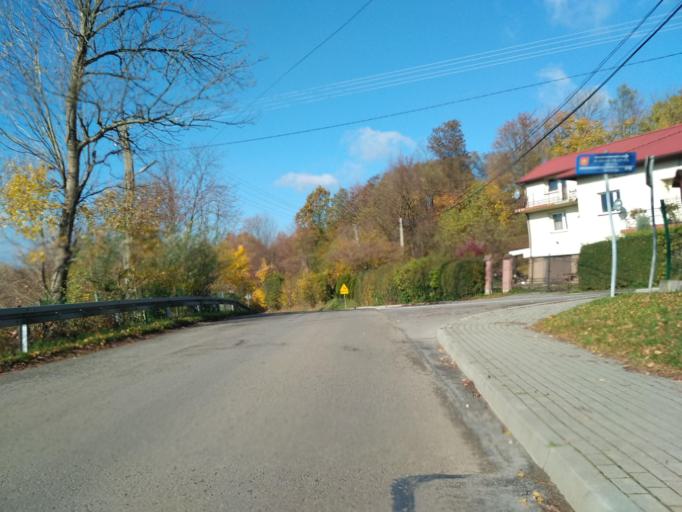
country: PL
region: Subcarpathian Voivodeship
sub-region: Powiat rzeszowski
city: Zglobien
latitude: 50.0247
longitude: 21.8801
